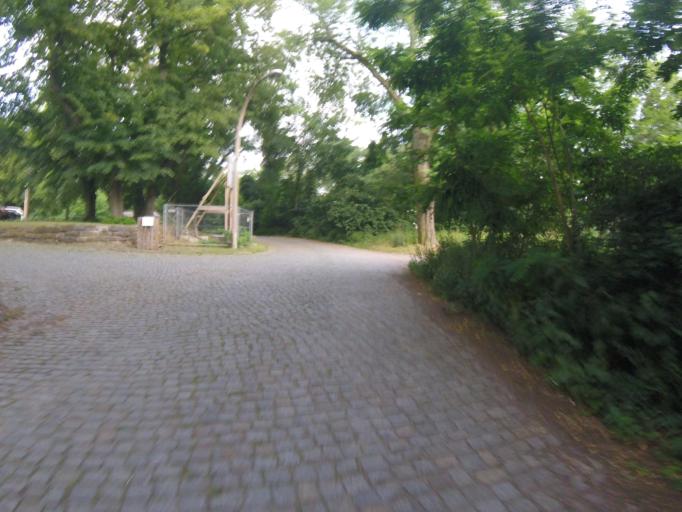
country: DE
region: Brandenburg
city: Konigs Wusterhausen
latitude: 52.3012
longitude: 13.6168
